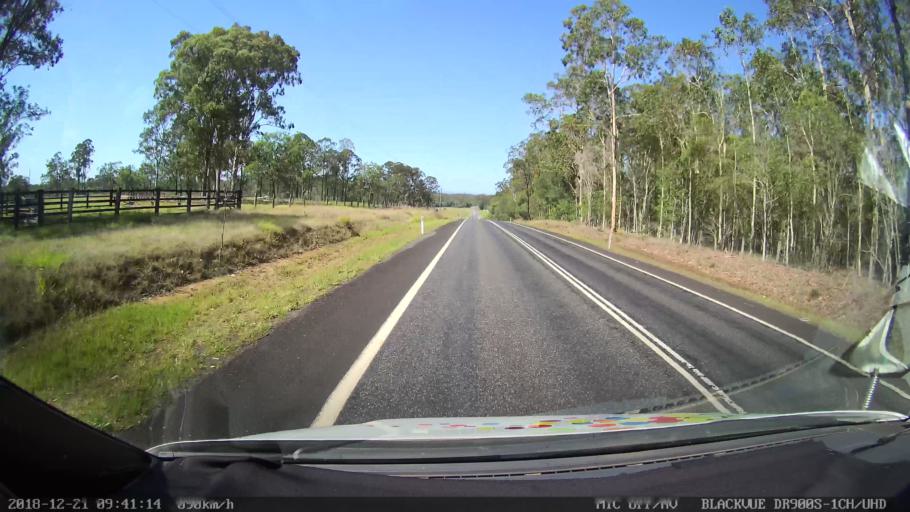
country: AU
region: New South Wales
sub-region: Clarence Valley
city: Grafton
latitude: -29.5828
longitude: 152.9592
